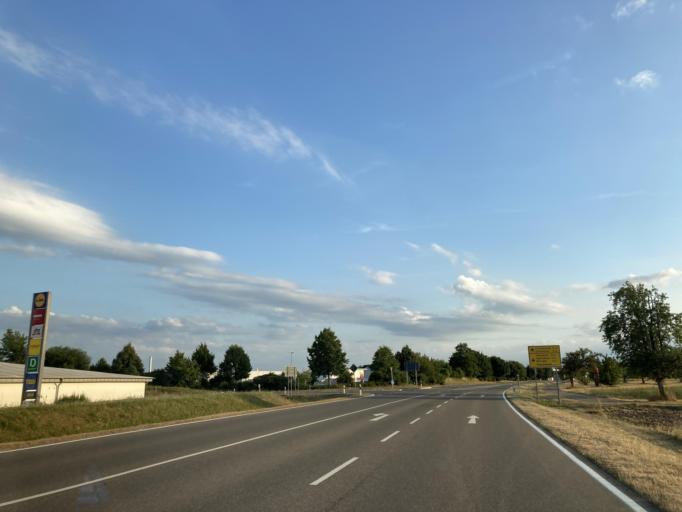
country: DE
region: Baden-Wuerttemberg
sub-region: Karlsruhe Region
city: Pfalzgrafenweiler
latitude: 48.5379
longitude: 8.5701
